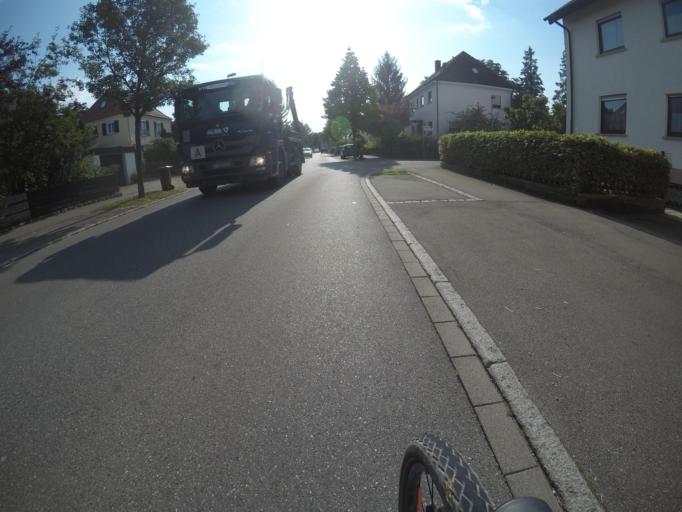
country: DE
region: Baden-Wuerttemberg
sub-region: Tuebingen Region
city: Metzingen
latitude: 48.5361
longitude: 9.2947
